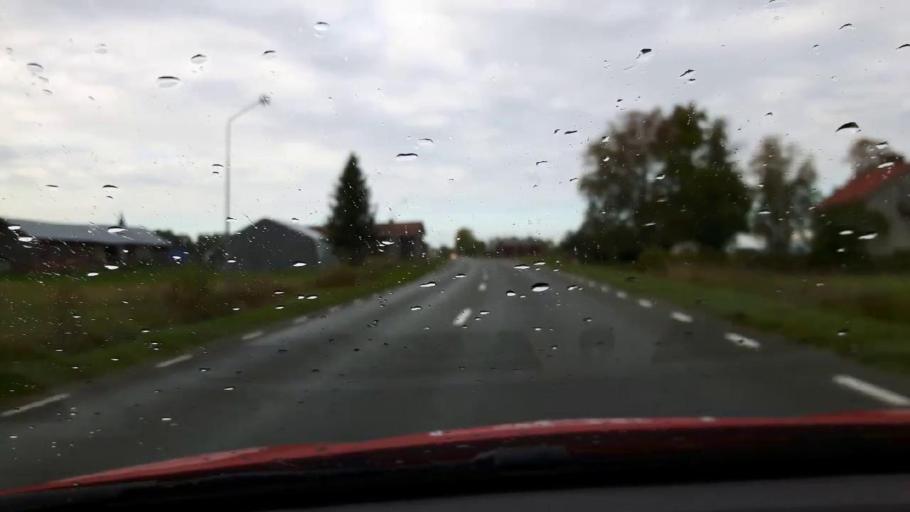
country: SE
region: Jaemtland
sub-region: Krokoms Kommun
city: Krokom
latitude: 63.1282
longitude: 14.2894
